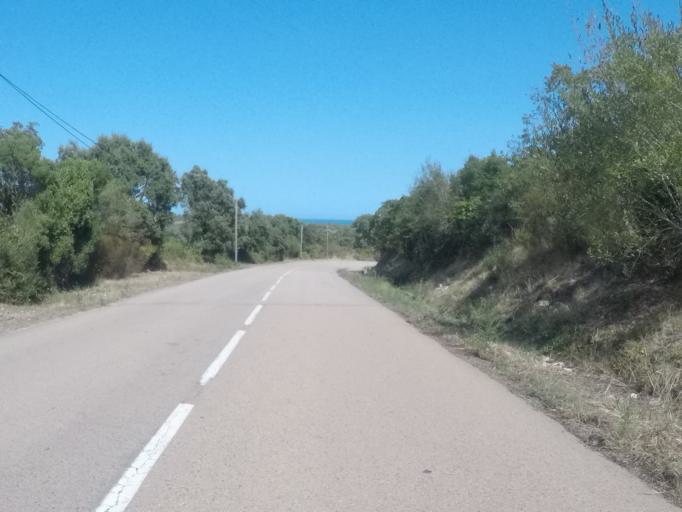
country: FR
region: Corsica
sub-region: Departement de la Corse-du-Sud
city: Sari-Solenzara
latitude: 41.8622
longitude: 9.3795
